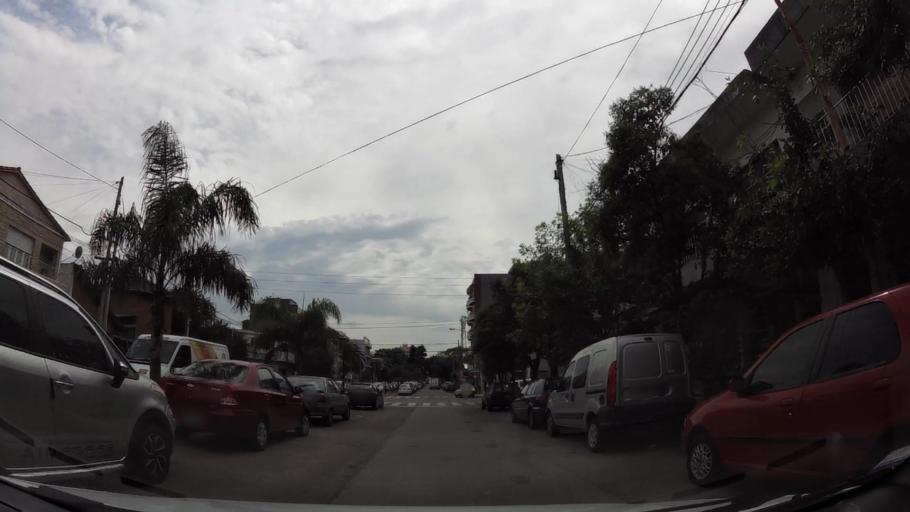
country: AR
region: Buenos Aires F.D.
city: Villa Lugano
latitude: -34.7004
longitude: -58.5094
